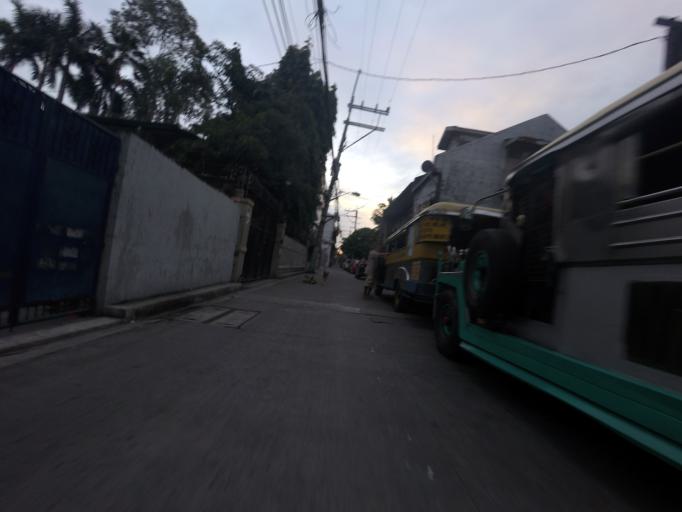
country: PH
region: Metro Manila
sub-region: San Juan
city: San Juan
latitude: 14.5997
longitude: 121.0297
